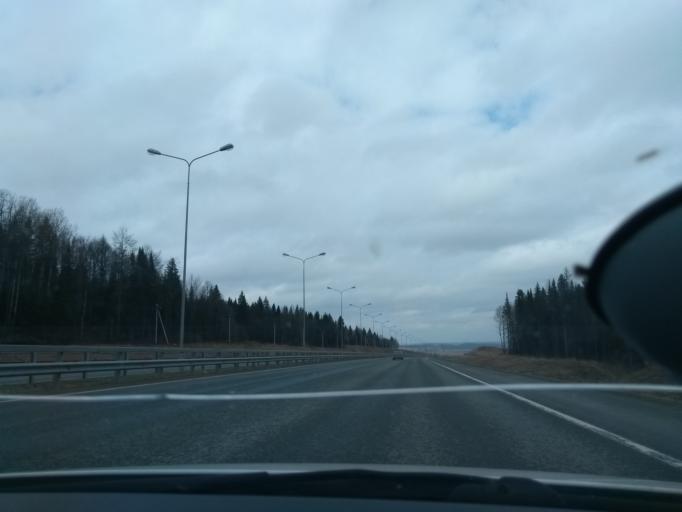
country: RU
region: Perm
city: Zvezdnyy
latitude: 57.7602
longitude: 56.3333
